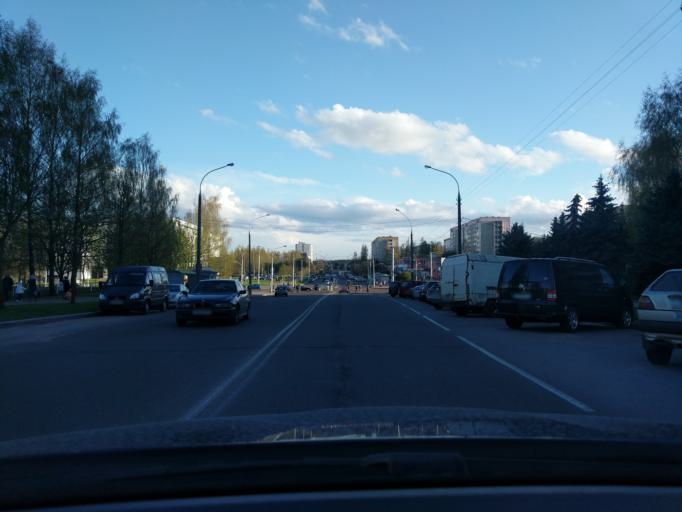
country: BY
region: Minsk
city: Novoye Medvezhino
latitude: 53.9000
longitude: 27.4531
